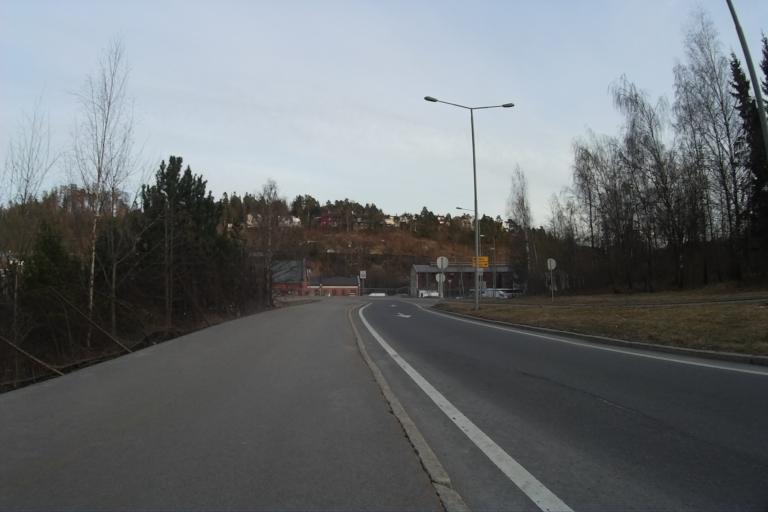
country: NO
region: Oslo
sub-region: Oslo
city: Oslo
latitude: 59.9109
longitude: 10.8192
